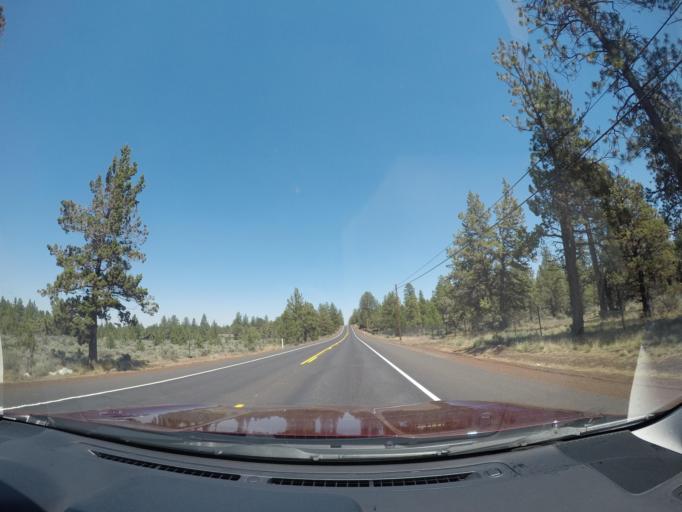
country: US
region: Oregon
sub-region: Deschutes County
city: Sisters
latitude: 44.2873
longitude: -121.5099
